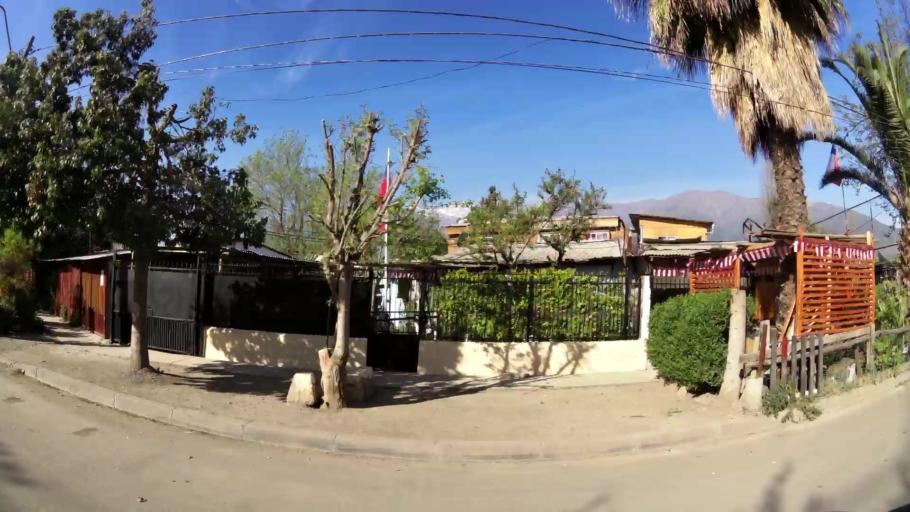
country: CL
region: Santiago Metropolitan
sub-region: Provincia de Santiago
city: Villa Presidente Frei, Nunoa, Santiago, Chile
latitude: -33.5150
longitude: -70.5590
